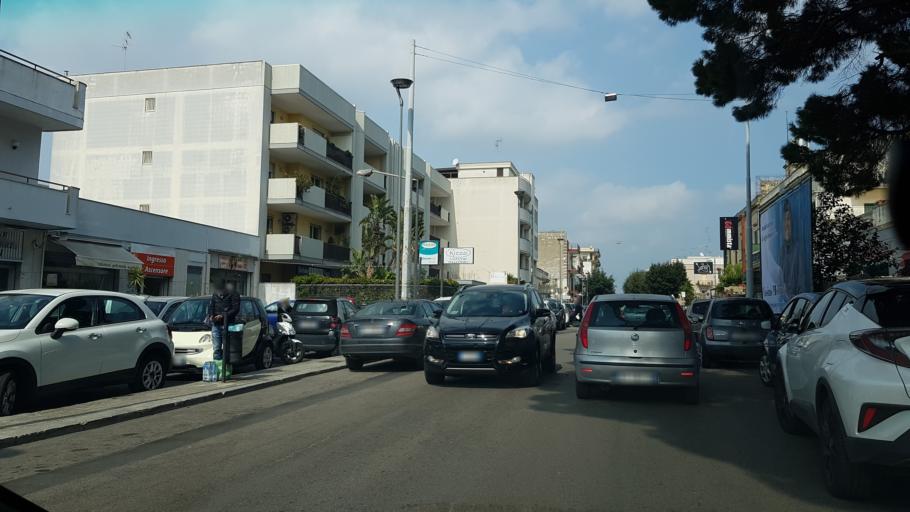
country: IT
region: Apulia
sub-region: Provincia di Lecce
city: Castromediano
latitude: 40.3374
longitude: 18.1778
